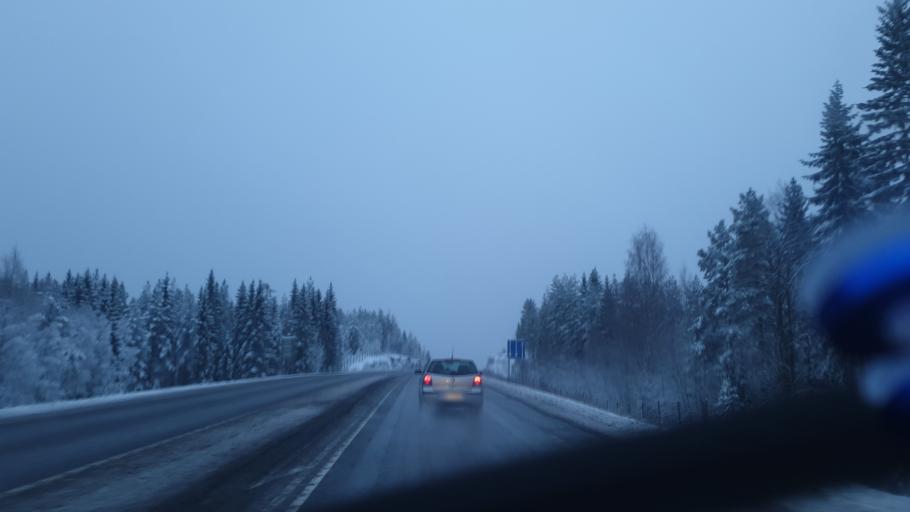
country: FI
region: Central Finland
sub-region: Saarijaervi-Viitasaari
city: Viitasaari
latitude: 63.0081
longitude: 25.8254
